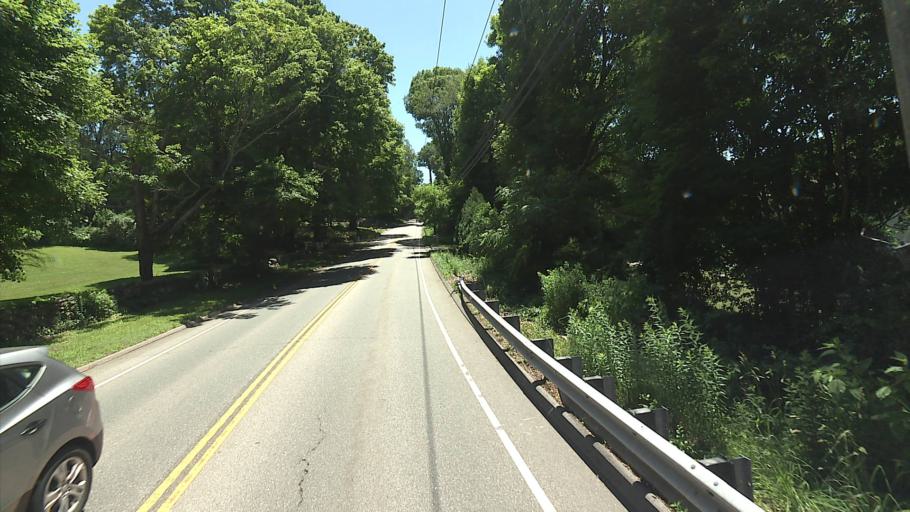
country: US
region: Connecticut
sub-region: New London County
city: Pawcatuck
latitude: 41.3822
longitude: -71.8552
